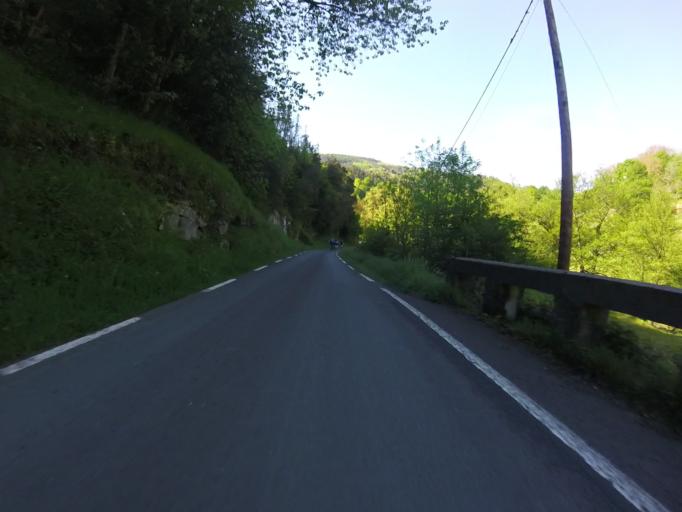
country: ES
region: Basque Country
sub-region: Provincia de Guipuzcoa
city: Errezil
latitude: 43.1767
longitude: -2.2043
